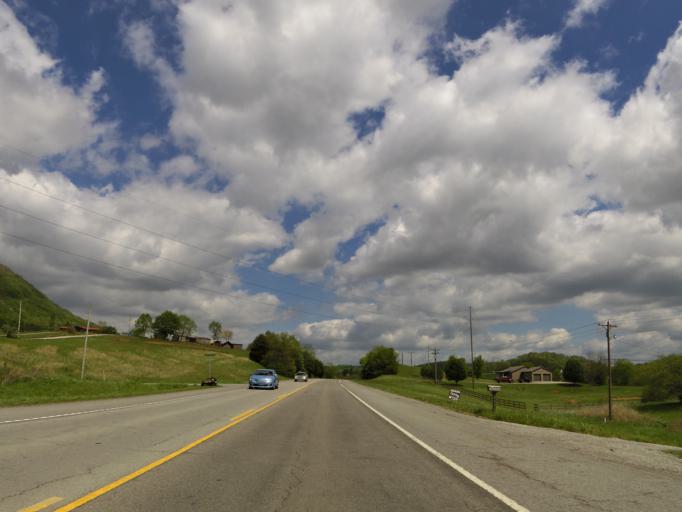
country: US
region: Tennessee
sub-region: Campbell County
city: Fincastle
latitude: 36.4586
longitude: -83.8944
